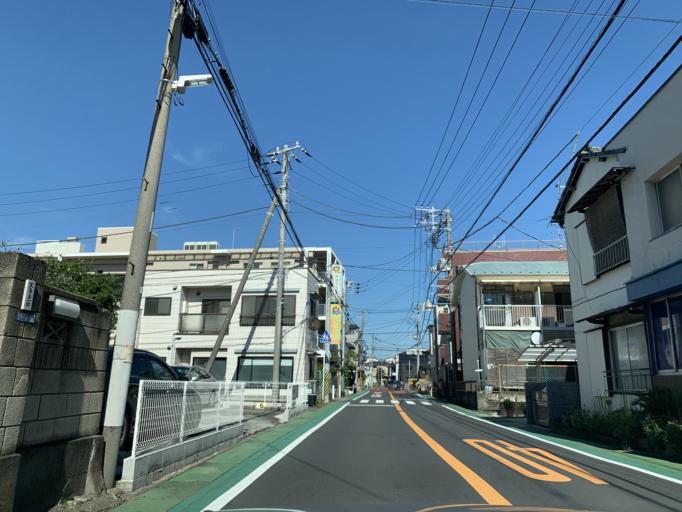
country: JP
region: Tokyo
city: Urayasu
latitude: 35.6871
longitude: 139.9124
